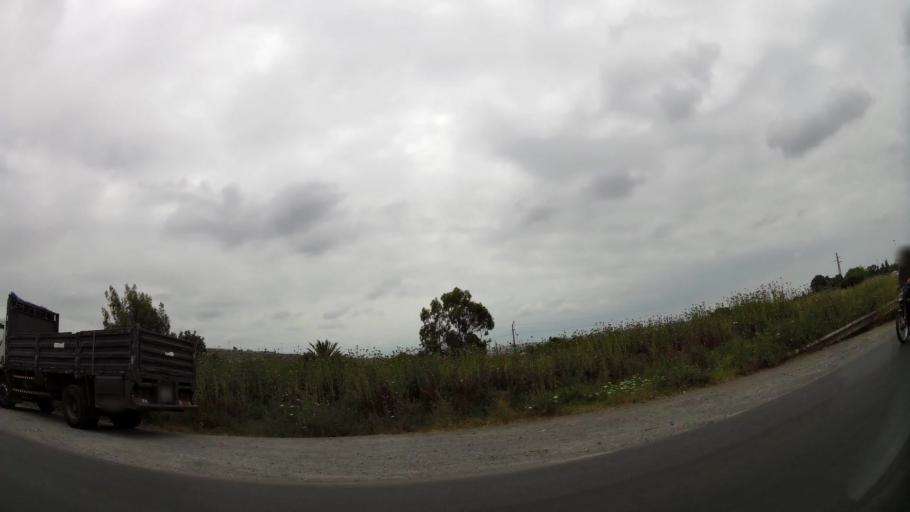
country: MA
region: Rabat-Sale-Zemmour-Zaer
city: Sale
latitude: 33.9902
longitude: -6.7633
